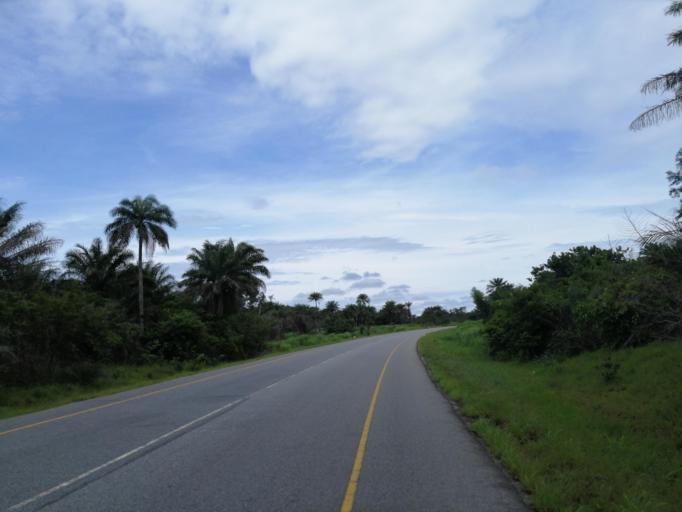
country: SL
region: Northern Province
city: Port Loko
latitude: 8.7571
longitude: -12.9122
